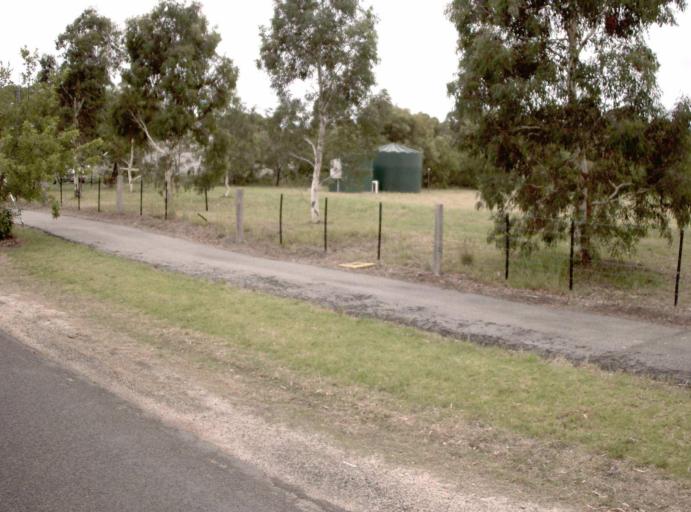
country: AU
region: Victoria
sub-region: Wellington
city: Sale
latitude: -37.8476
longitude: 147.0718
